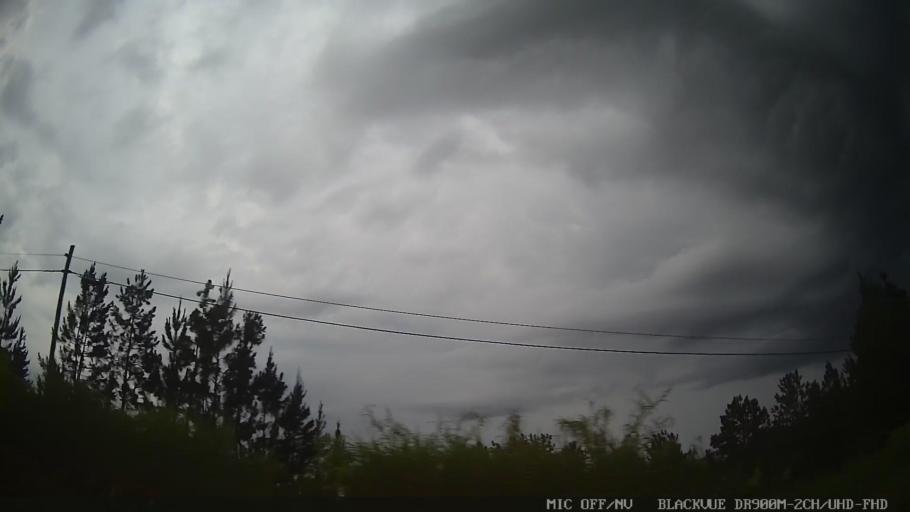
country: BR
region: Sao Paulo
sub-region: Amparo
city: Amparo
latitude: -22.7425
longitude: -46.7596
